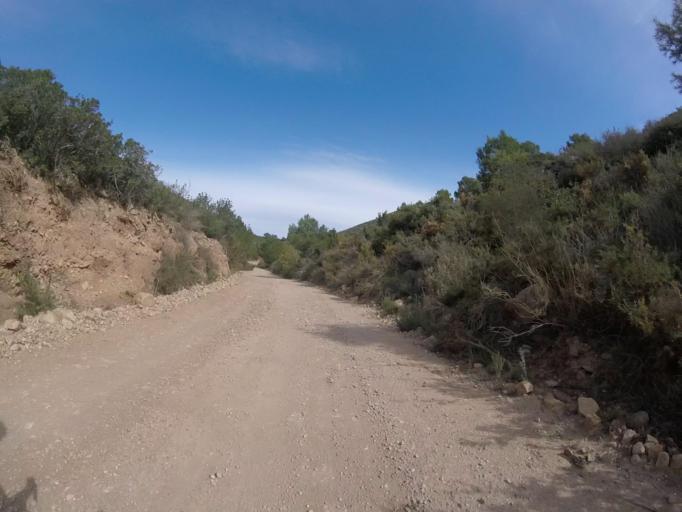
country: ES
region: Valencia
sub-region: Provincia de Castello
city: Torreblanca
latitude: 40.1988
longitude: 0.1546
